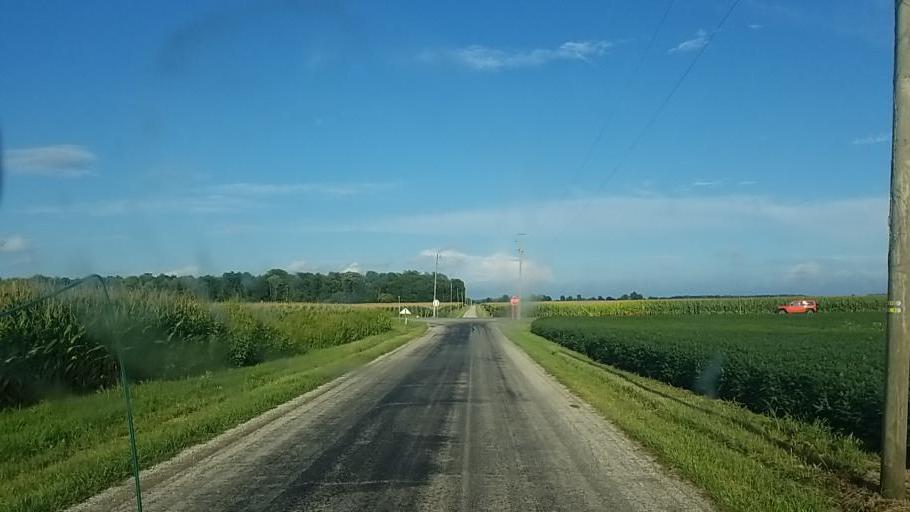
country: US
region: Ohio
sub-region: Crawford County
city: Bucyrus
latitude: 40.7466
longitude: -82.9928
